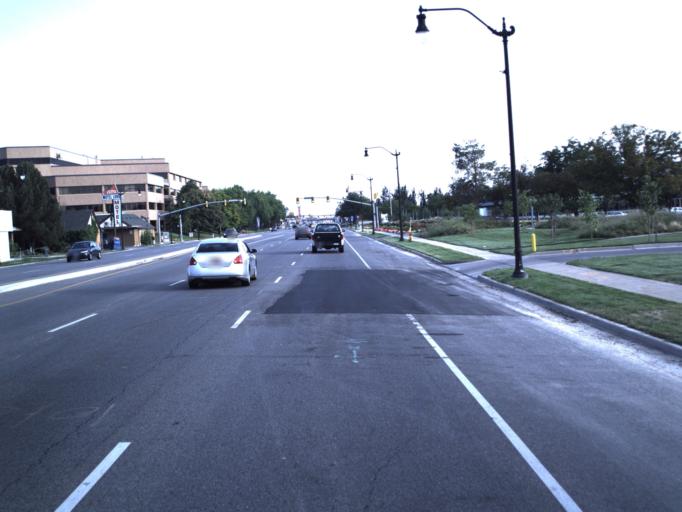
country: US
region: Utah
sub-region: Salt Lake County
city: South Salt Lake
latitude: 40.7302
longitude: -111.8884
